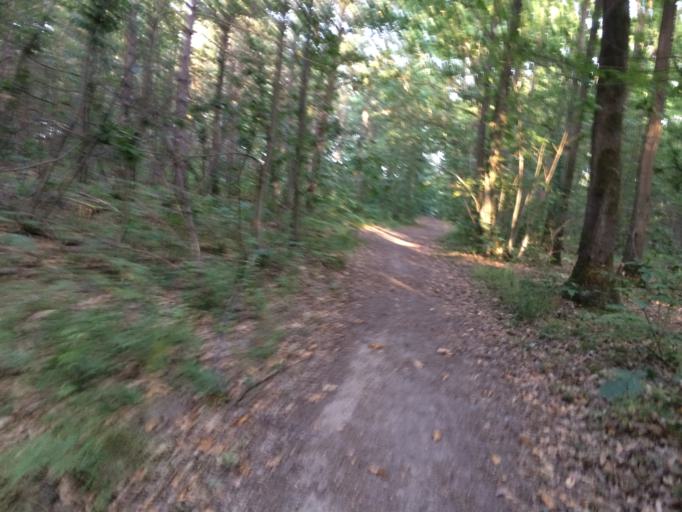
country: FR
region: Ile-de-France
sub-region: Departement de l'Essonne
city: Igny
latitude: 48.7450
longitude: 2.2450
